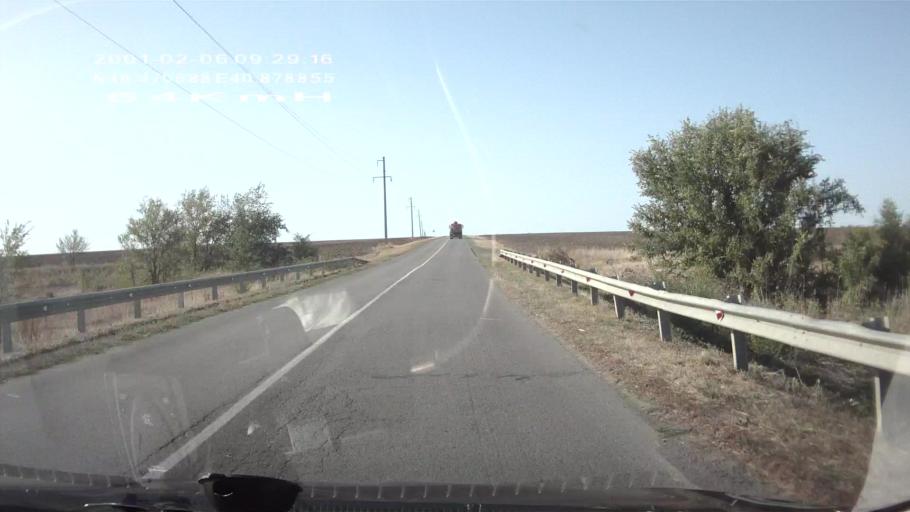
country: RU
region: Rostov
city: Tselina
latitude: 46.4705
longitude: 40.8785
